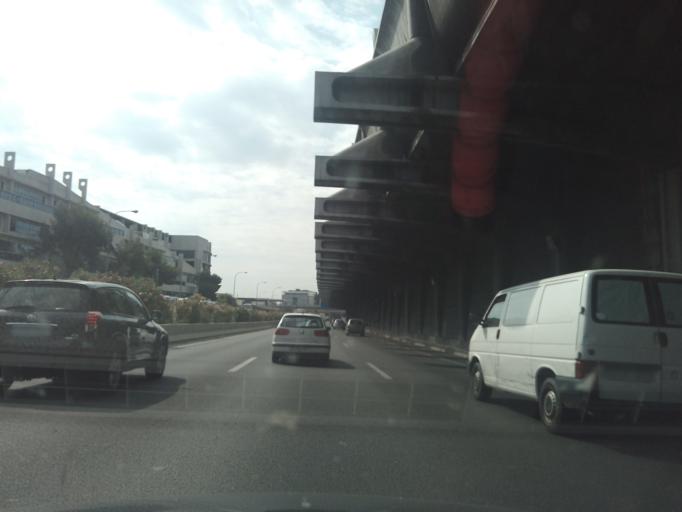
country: ES
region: Madrid
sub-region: Provincia de Madrid
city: Hortaleza
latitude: 40.4725
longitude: -3.6322
